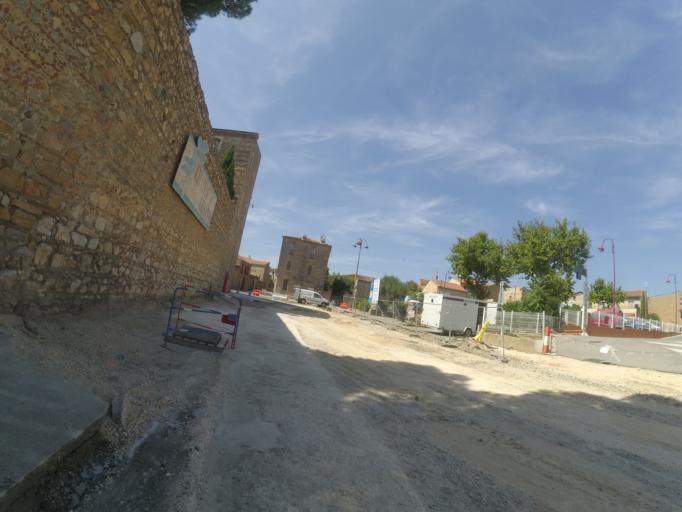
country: FR
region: Languedoc-Roussillon
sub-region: Departement des Pyrenees-Orientales
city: Baixas
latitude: 42.7513
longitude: 2.8121
